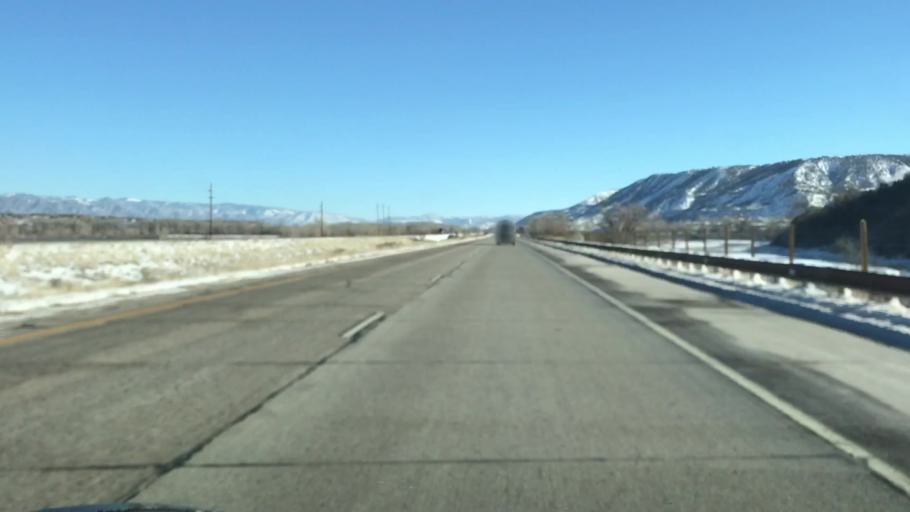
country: US
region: Colorado
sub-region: Garfield County
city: Rifle
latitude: 39.5195
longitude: -107.8190
